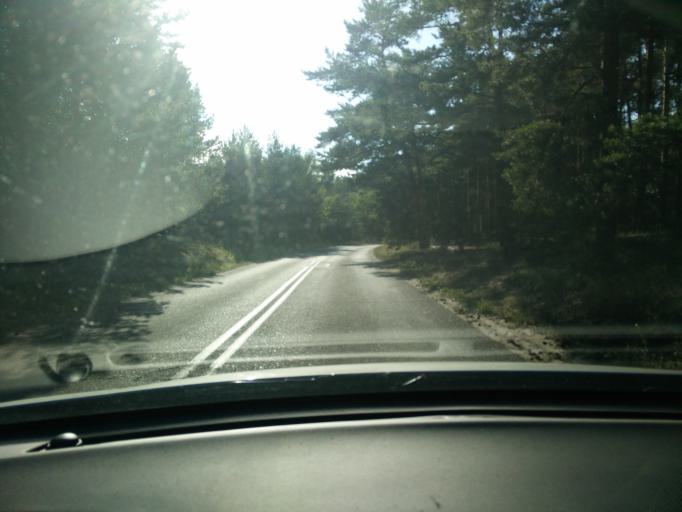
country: PL
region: Pomeranian Voivodeship
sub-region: Powiat pucki
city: Hel
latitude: 54.6484
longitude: 18.7675
